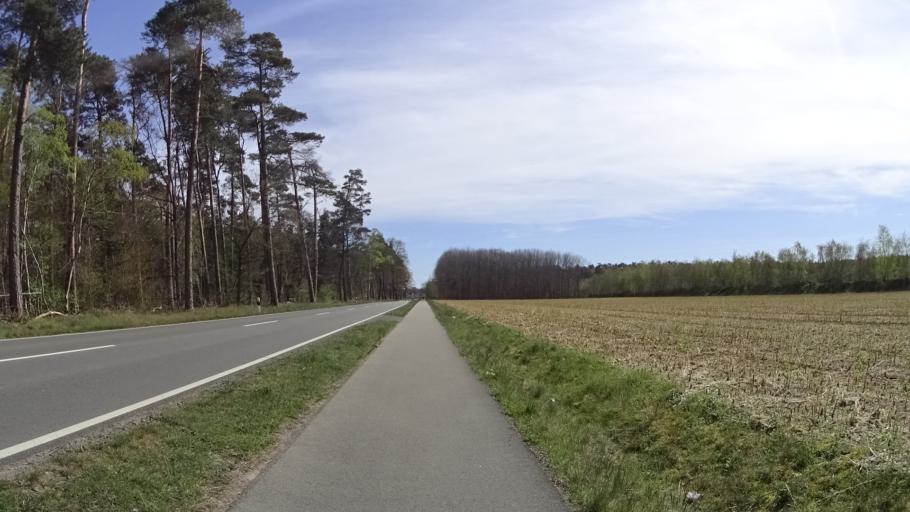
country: DE
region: Lower Saxony
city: Spelle
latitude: 52.3410
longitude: 7.4495
